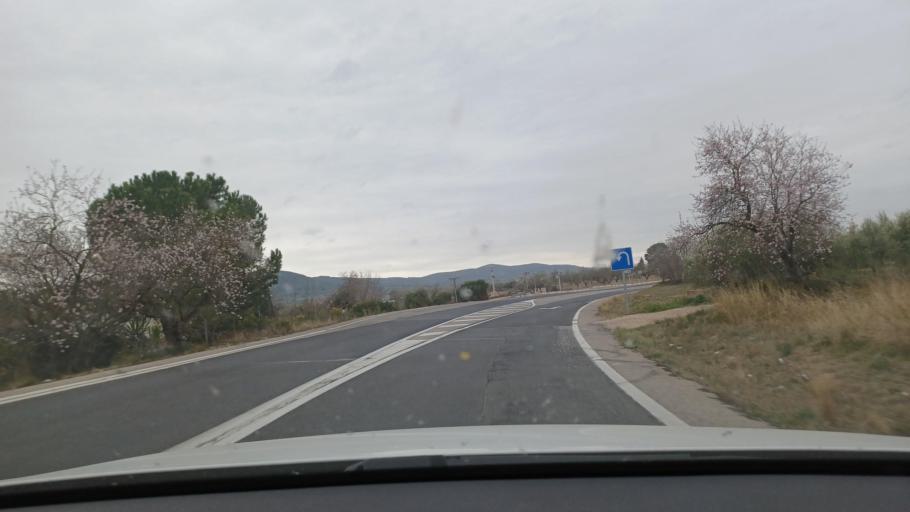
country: ES
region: Catalonia
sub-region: Provincia de Tarragona
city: Santa Barbara
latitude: 40.6794
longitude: 0.4580
